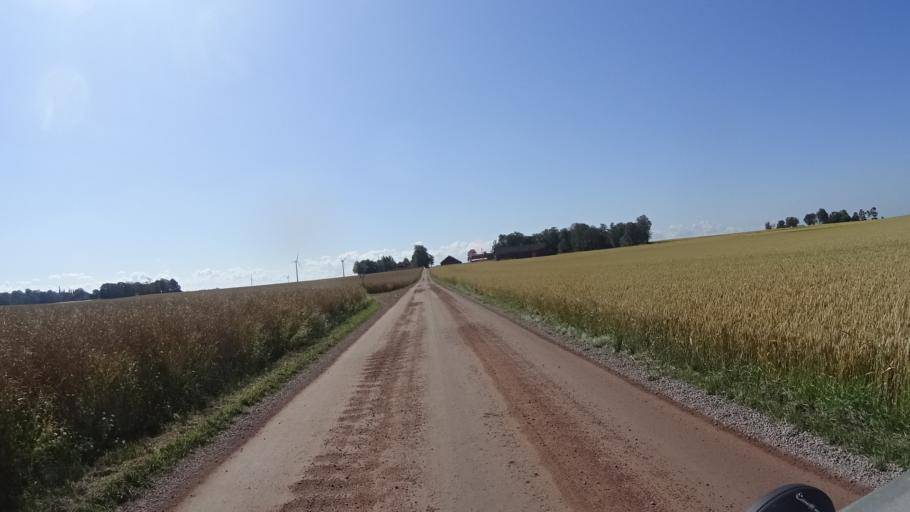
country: SE
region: OEstergoetland
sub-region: Vadstena Kommun
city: Herrestad
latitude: 58.3288
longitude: 14.8241
